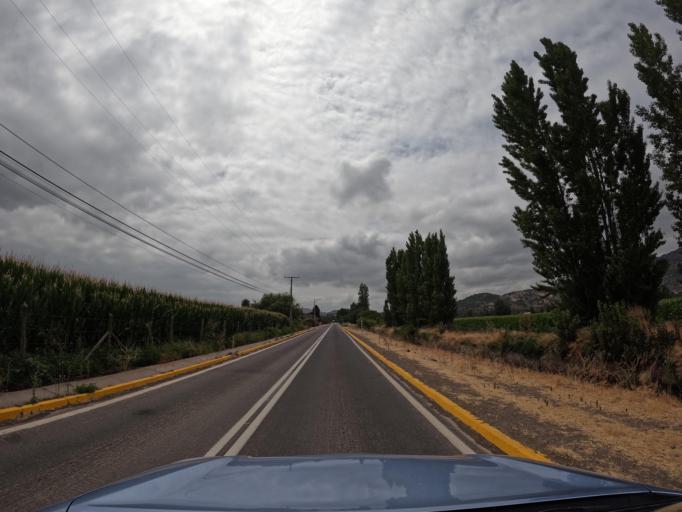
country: CL
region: Maule
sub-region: Provincia de Curico
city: Teno
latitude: -34.7769
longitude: -71.1791
